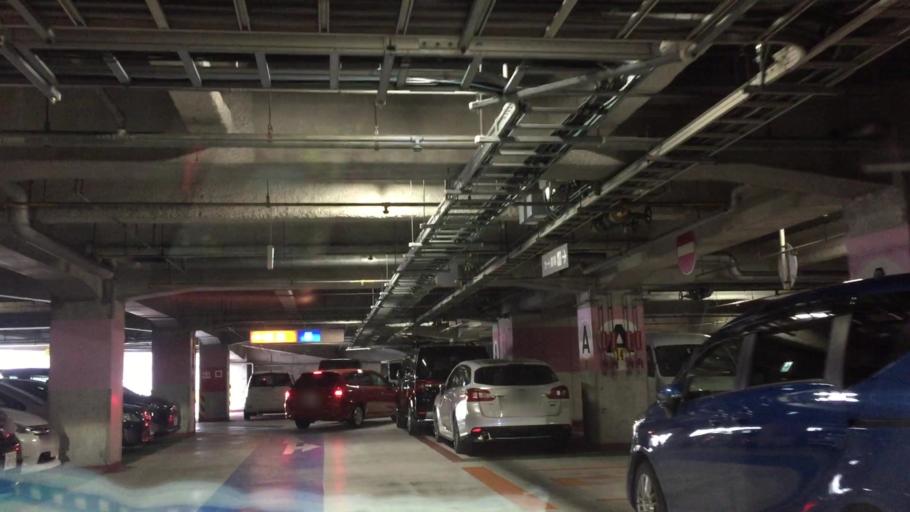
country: JP
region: Kanagawa
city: Zushi
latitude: 35.3349
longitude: 139.6238
